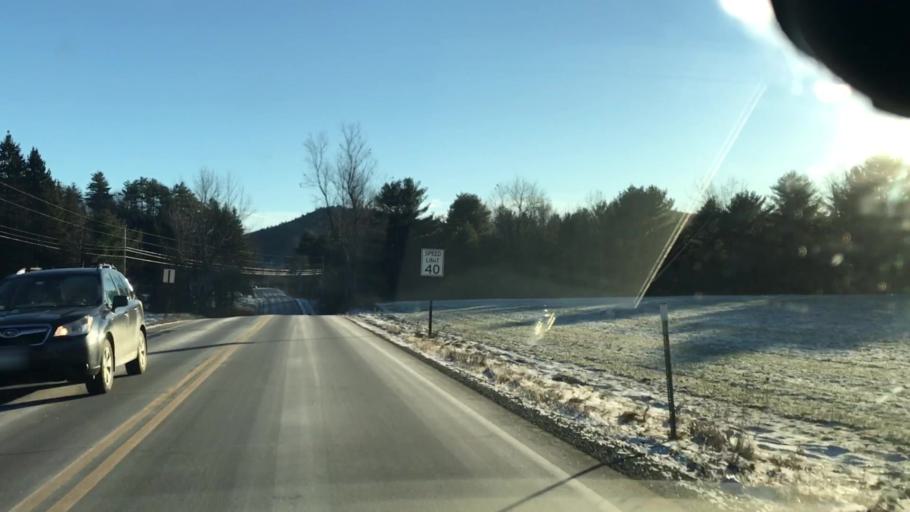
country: US
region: New Hampshire
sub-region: Grafton County
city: Lyme Town Offices
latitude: 43.8511
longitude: -72.1562
